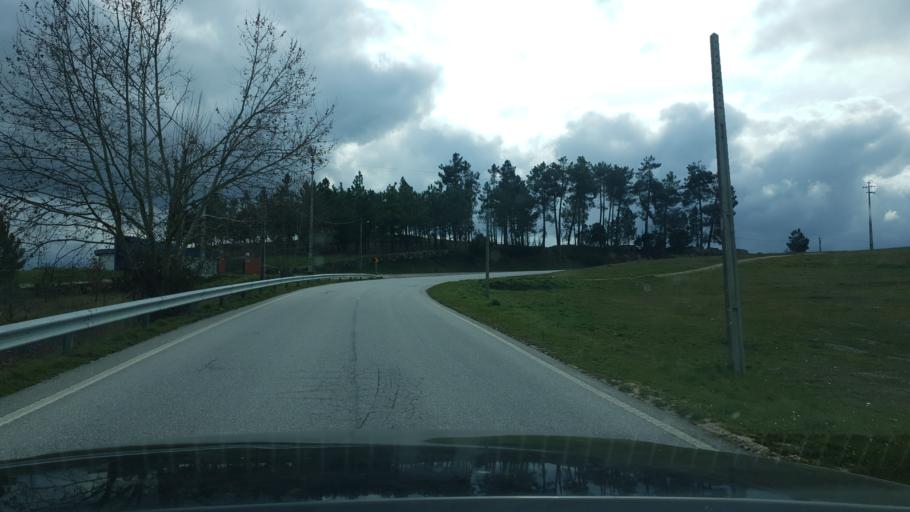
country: PT
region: Viseu
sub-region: Moimenta da Beira
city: Moimenta da Beira
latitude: 40.9558
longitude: -7.5826
